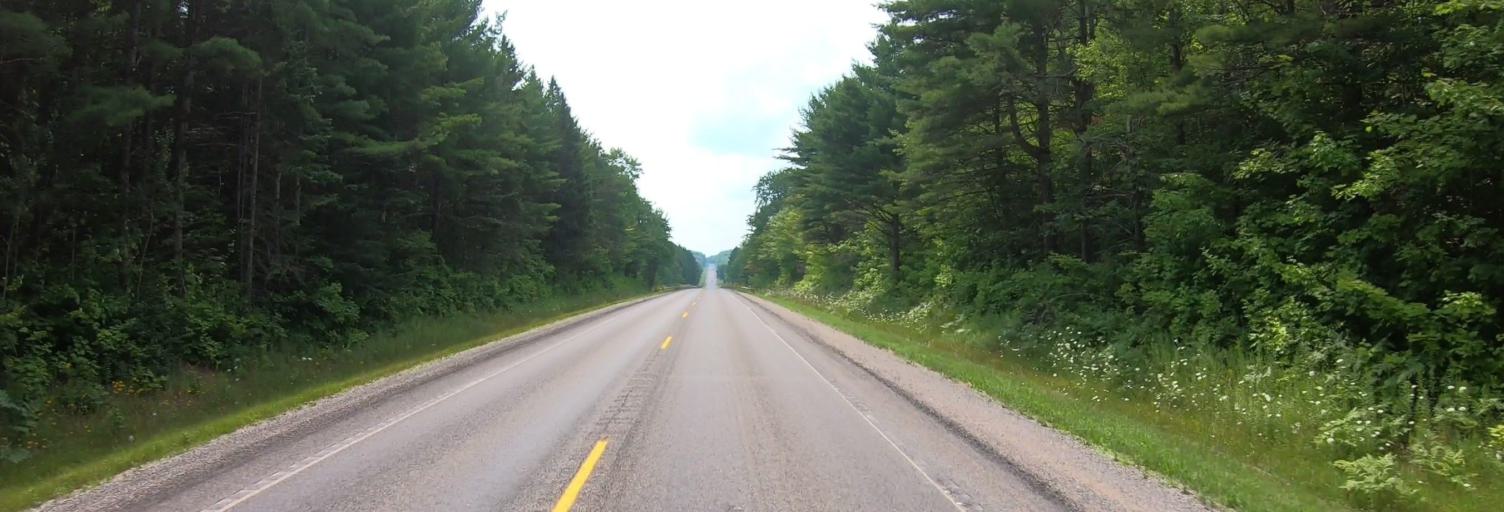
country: US
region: Michigan
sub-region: Alger County
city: Munising
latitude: 46.3684
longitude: -86.7087
